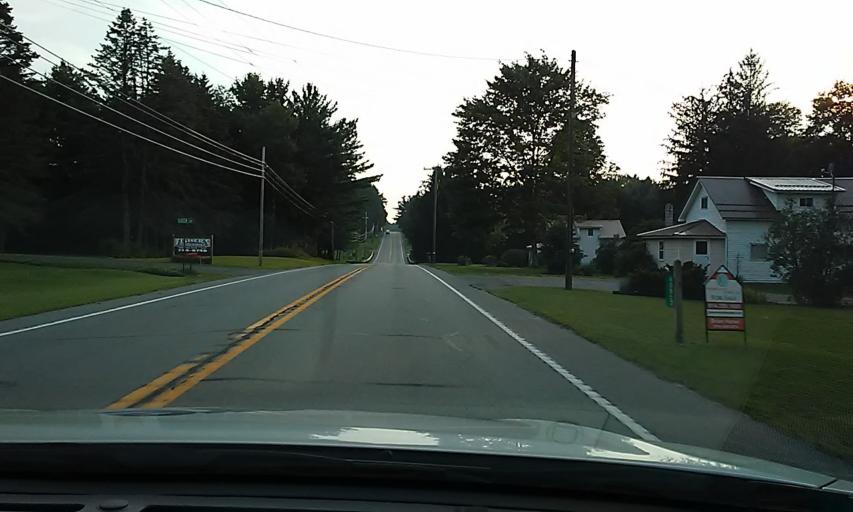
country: US
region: Pennsylvania
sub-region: Forest County
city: Marienville
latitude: 41.4568
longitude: -79.1485
